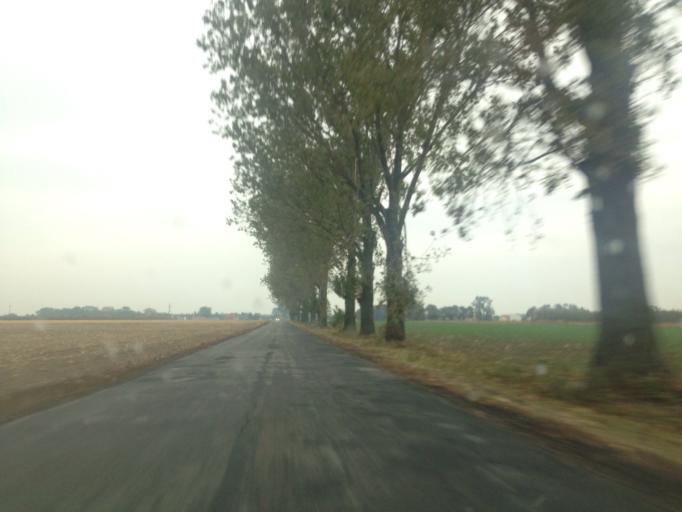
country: PL
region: Greater Poland Voivodeship
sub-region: Powiat poznanski
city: Kleszczewo
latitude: 52.3540
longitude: 17.1428
